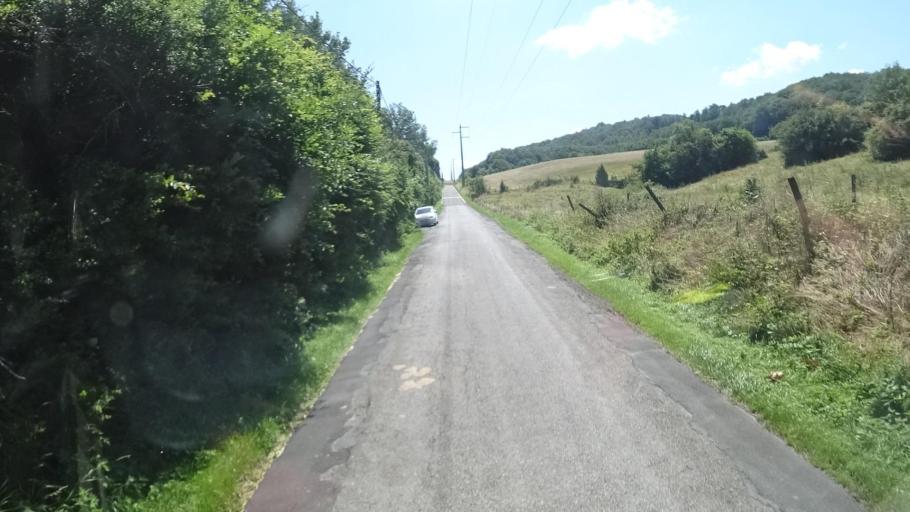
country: BE
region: Wallonia
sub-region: Province de Namur
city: Profondeville
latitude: 50.3607
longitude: 4.8235
